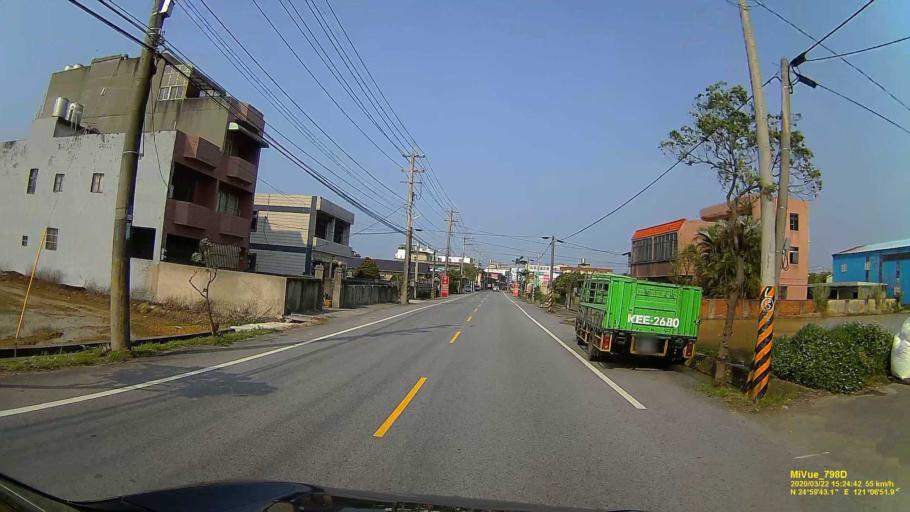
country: TW
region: Taiwan
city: Taoyuan City
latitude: 24.9955
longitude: 121.1144
